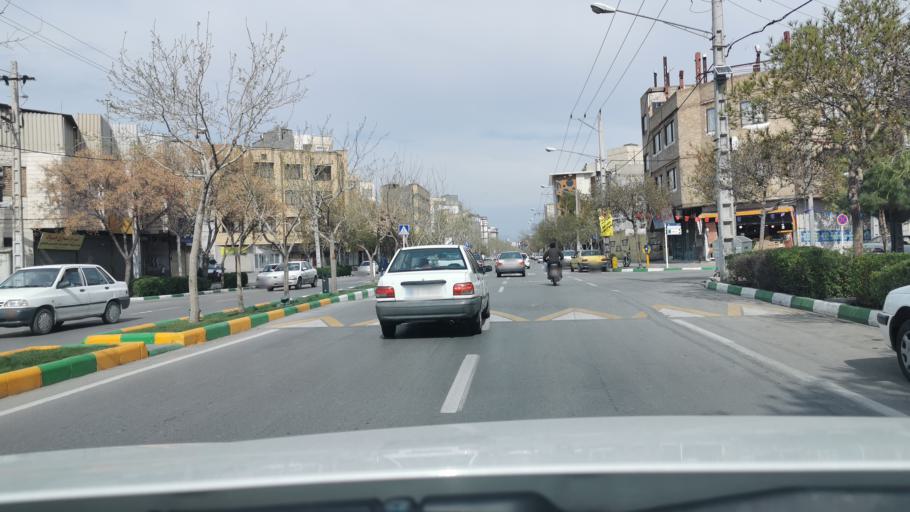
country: IR
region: Razavi Khorasan
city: Mashhad
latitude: 36.3150
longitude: 59.5953
